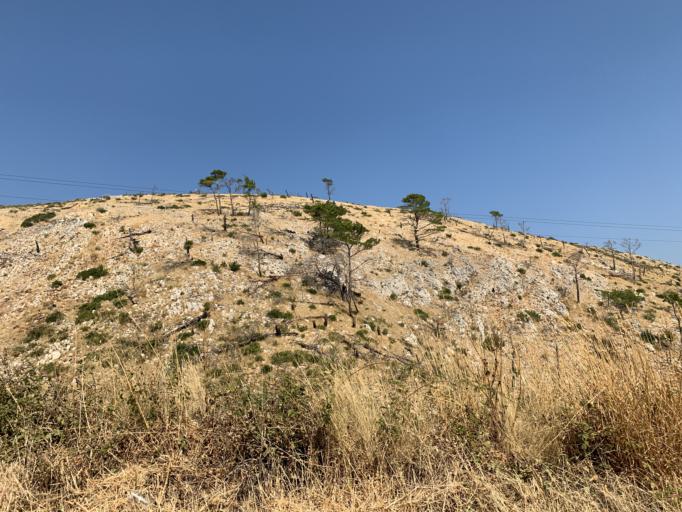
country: GR
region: North Aegean
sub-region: Chios
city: Thymiana
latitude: 38.3140
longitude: 26.0053
